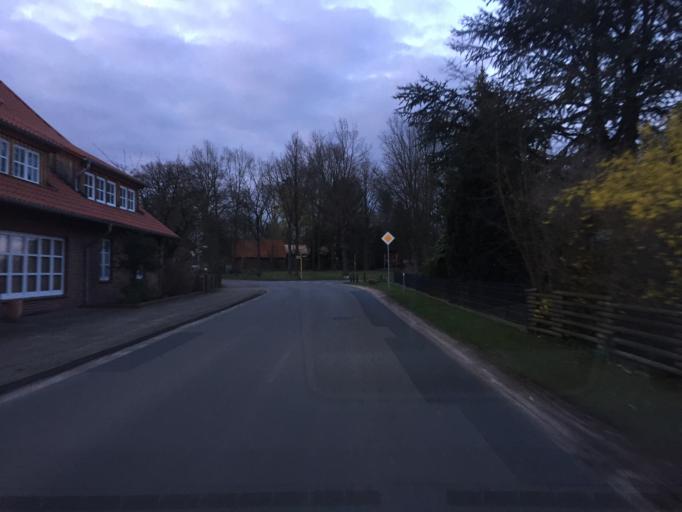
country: DE
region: Lower Saxony
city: Steimbke
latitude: 52.5978
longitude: 9.3963
